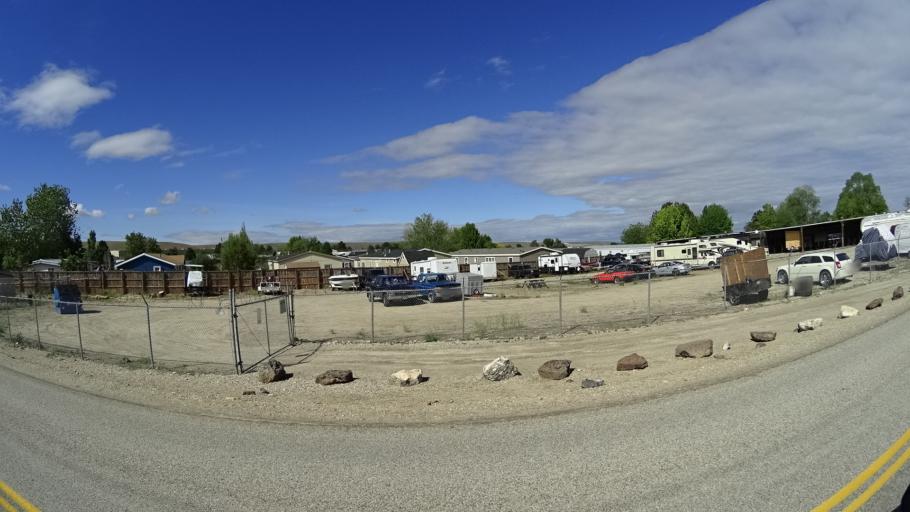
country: US
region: Idaho
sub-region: Ada County
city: Boise
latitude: 43.5265
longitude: -116.1547
